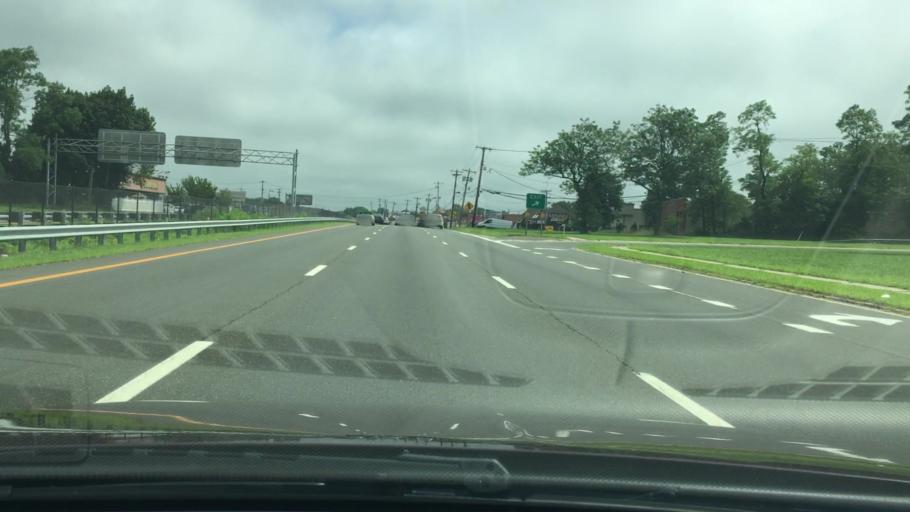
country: US
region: New York
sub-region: Suffolk County
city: Copiague
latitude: 40.6907
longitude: -73.4026
